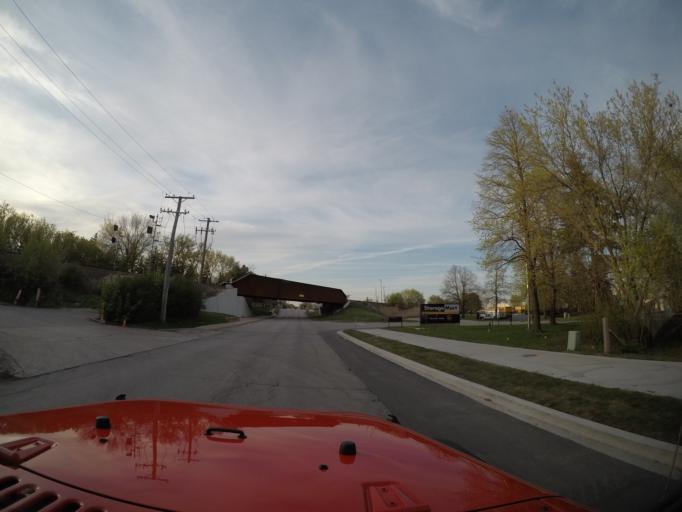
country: US
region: Illinois
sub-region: Cook County
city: Northbrook
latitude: 42.1027
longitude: -87.8294
